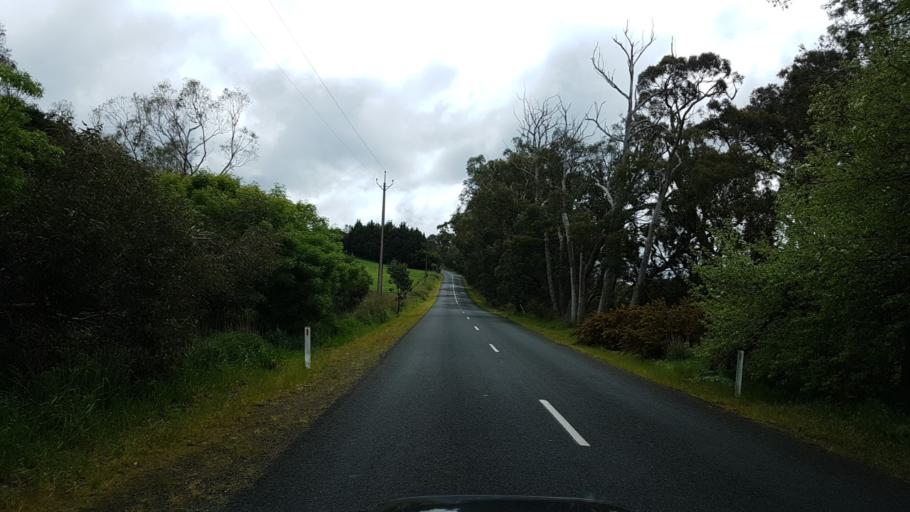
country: AU
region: South Australia
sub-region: Adelaide Hills
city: Lobethal
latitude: -34.8919
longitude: 138.8930
